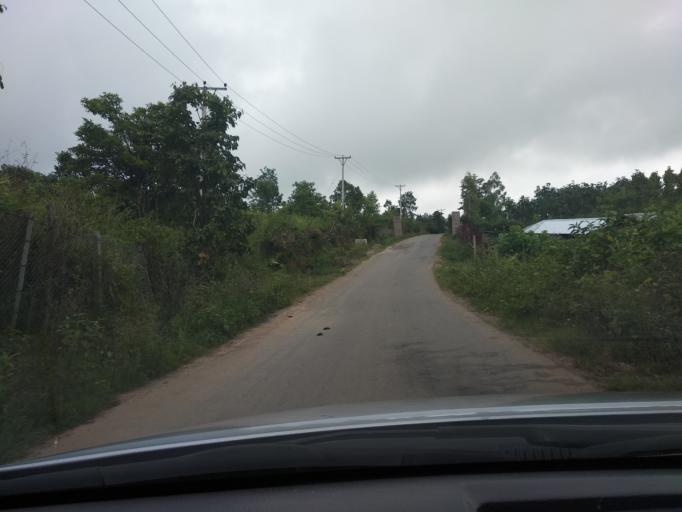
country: MM
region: Mandalay
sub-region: Pyin Oo Lwin District
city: Pyin Oo Lwin
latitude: 21.9168
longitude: 96.3837
